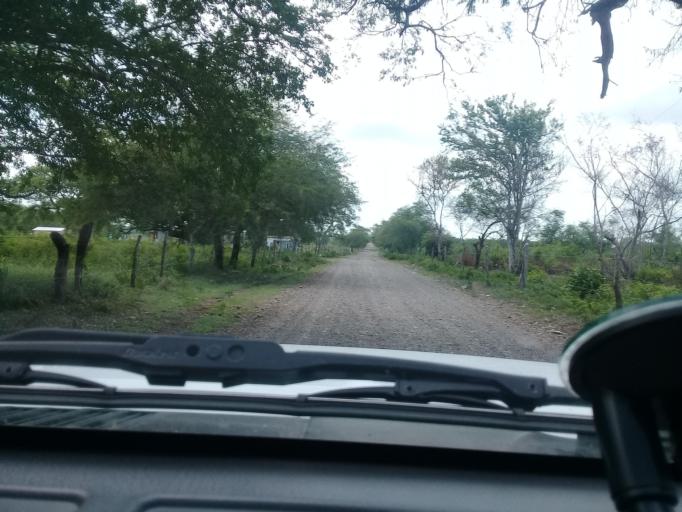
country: MX
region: Veracruz
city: Moralillo
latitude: 22.1592
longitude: -97.9906
